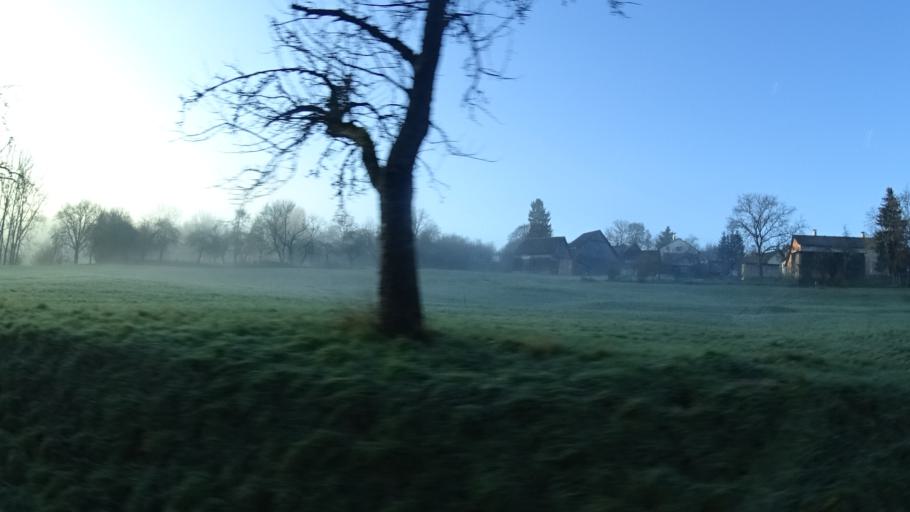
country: DE
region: Bavaria
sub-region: Regierungsbezirk Unterfranken
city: Eichenbuhl
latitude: 49.6662
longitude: 9.3617
